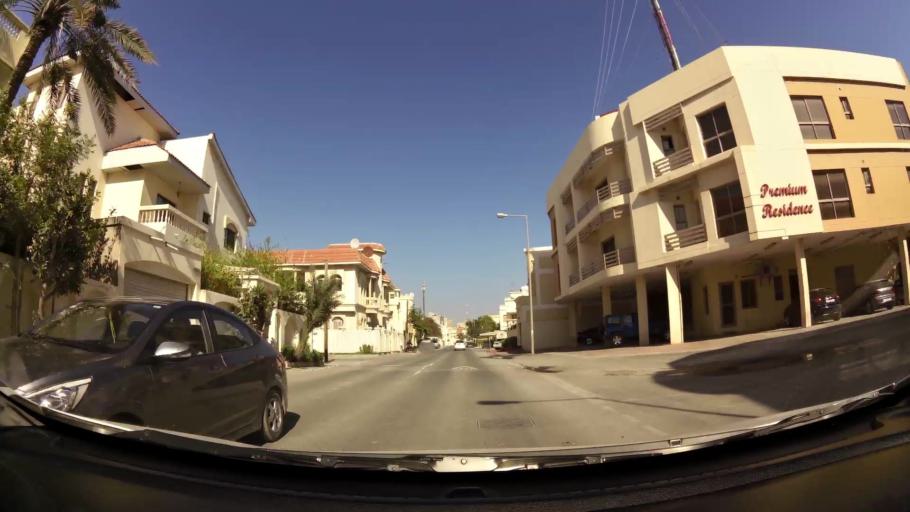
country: BH
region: Manama
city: Manama
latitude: 26.2088
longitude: 50.5708
